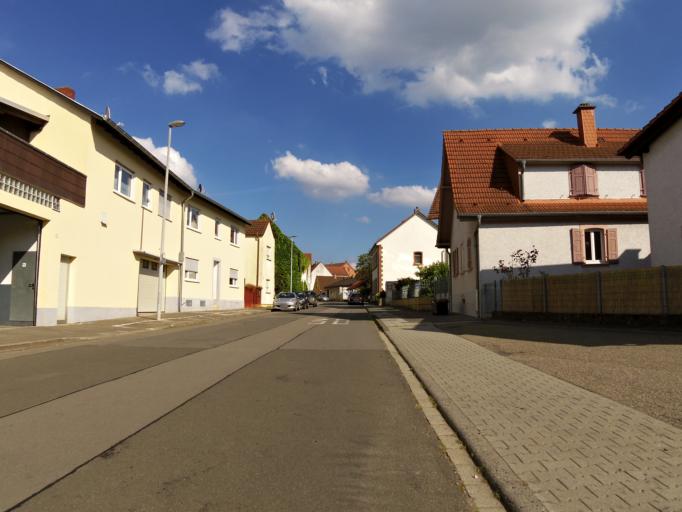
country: DE
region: Rheinland-Pfalz
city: Wattenheim
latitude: 49.5215
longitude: 8.0562
